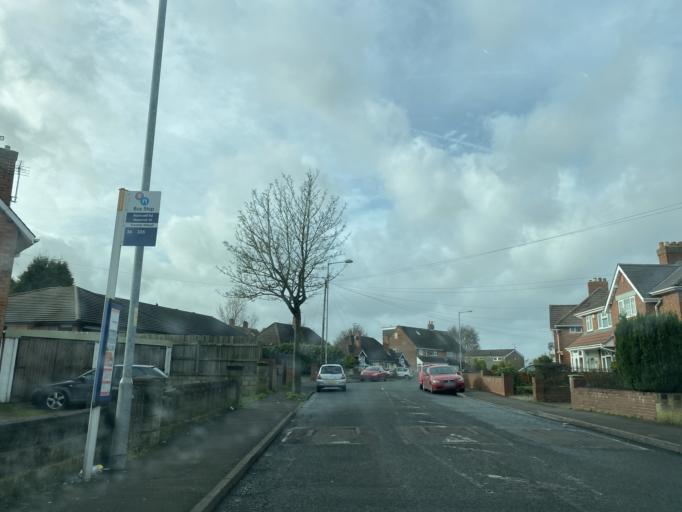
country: GB
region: England
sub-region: Walsall
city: Walsall
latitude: 52.5812
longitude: -2.0026
